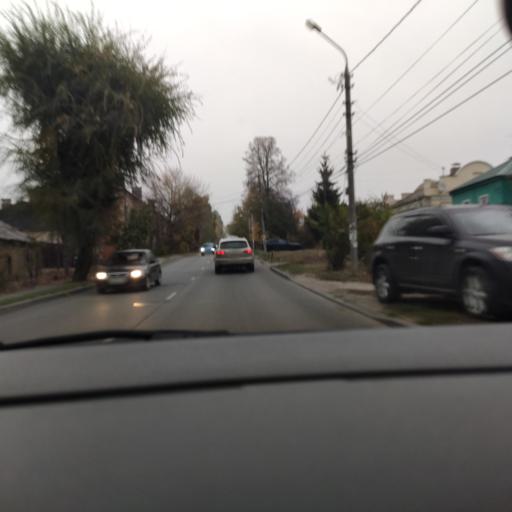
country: RU
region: Voronezj
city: Voronezh
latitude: 51.6923
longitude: 39.1903
